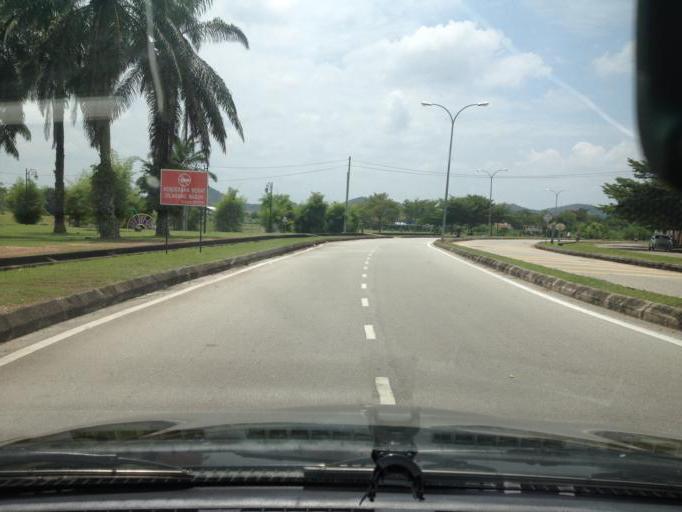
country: MY
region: Kedah
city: Sungai Petani
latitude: 5.6055
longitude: 100.5465
